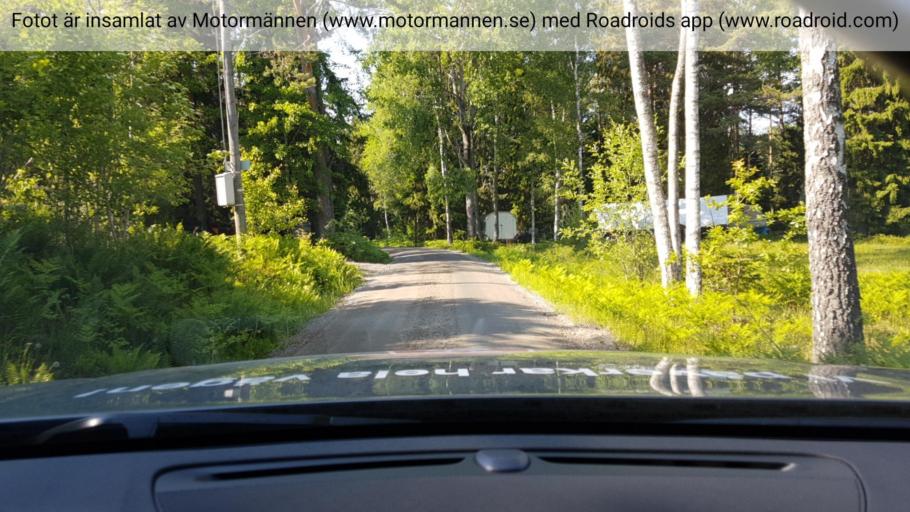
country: SE
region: Stockholm
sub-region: Varmdo Kommun
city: Mortnas
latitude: 59.2474
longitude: 18.4575
